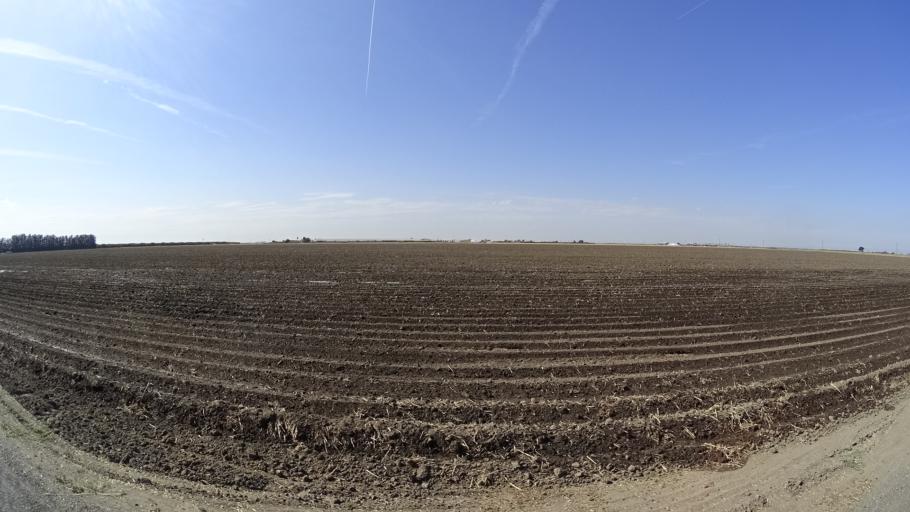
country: US
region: California
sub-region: Kings County
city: Home Garden
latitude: 36.2261
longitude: -119.5347
